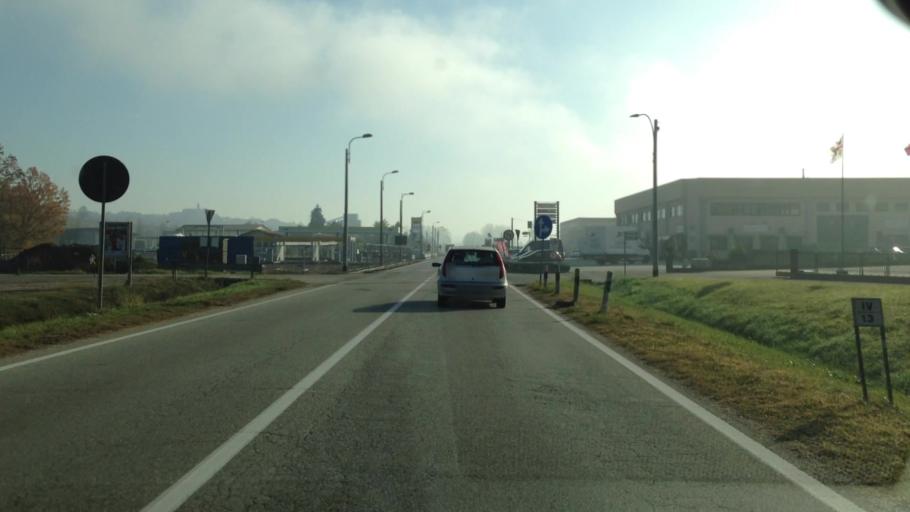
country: IT
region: Piedmont
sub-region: Provincia di Asti
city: Vigliano d'Asti
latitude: 44.8269
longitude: 8.2099
